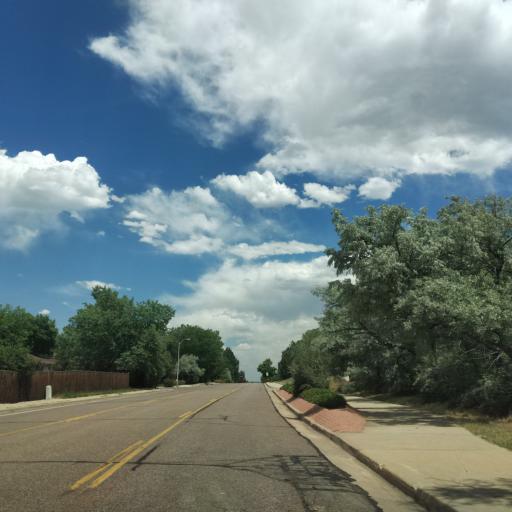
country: US
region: Colorado
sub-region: Jefferson County
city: Lakewood
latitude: 39.6893
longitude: -105.1105
